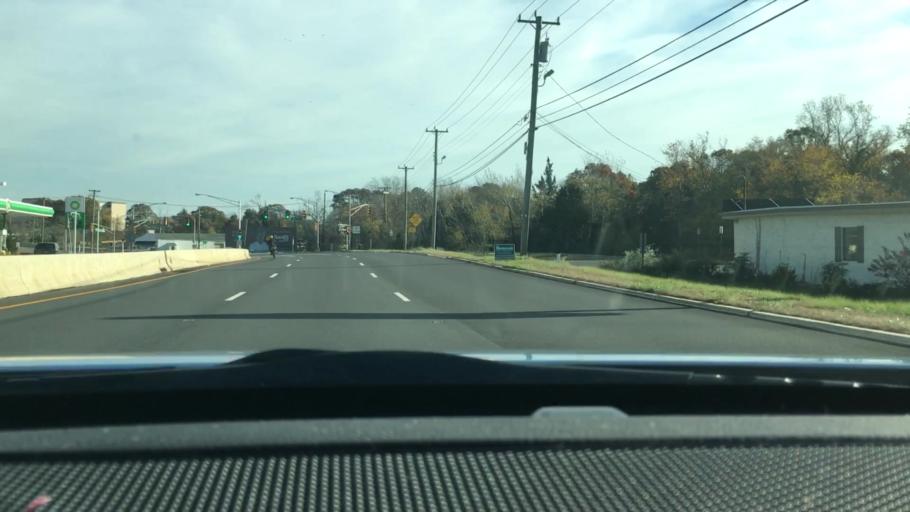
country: US
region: New Jersey
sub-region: Atlantic County
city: Absecon
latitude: 39.4209
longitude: -74.4981
